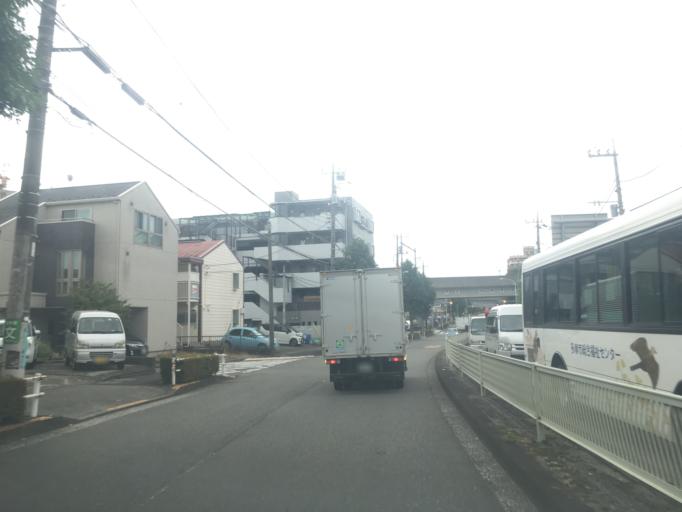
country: JP
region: Tokyo
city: Hino
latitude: 35.6245
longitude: 139.4178
